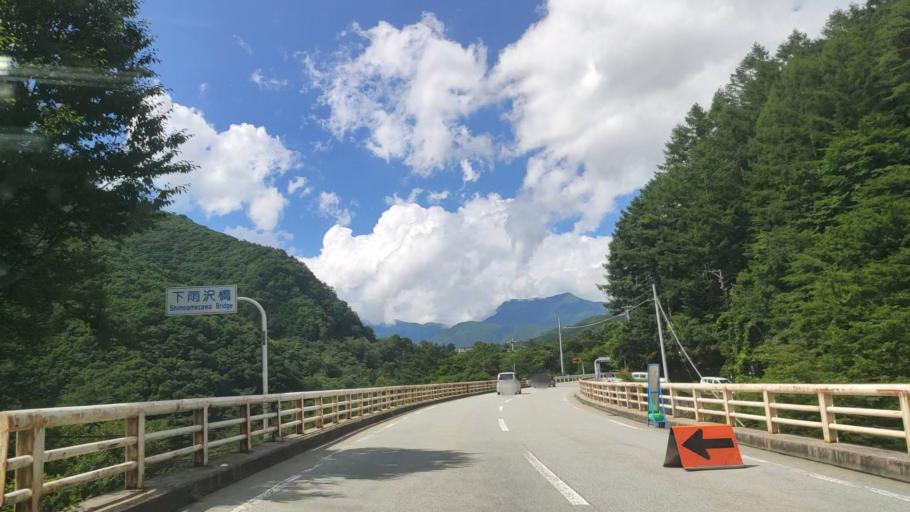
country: JP
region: Yamanashi
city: Enzan
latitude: 35.8317
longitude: 138.7642
